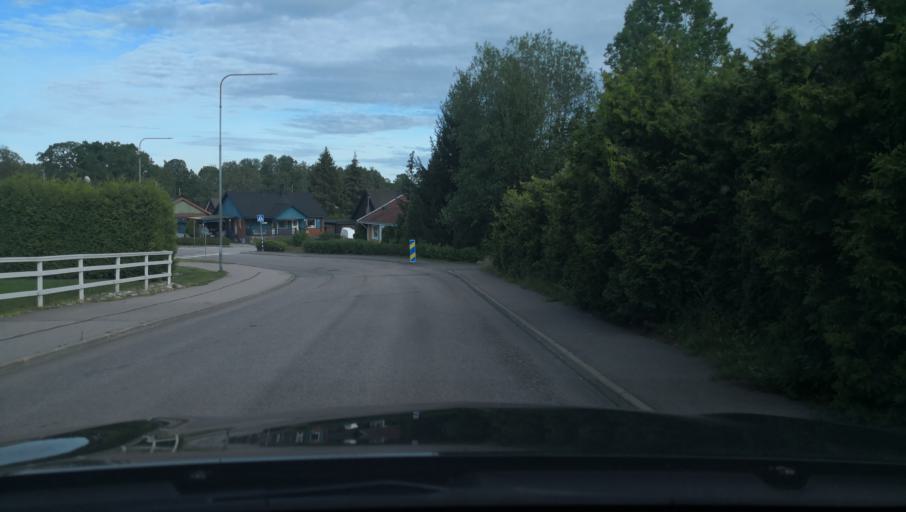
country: SE
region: Vaestmanland
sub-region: Hallstahammars Kommun
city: Hallstahammar
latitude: 59.6190
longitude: 16.2021
